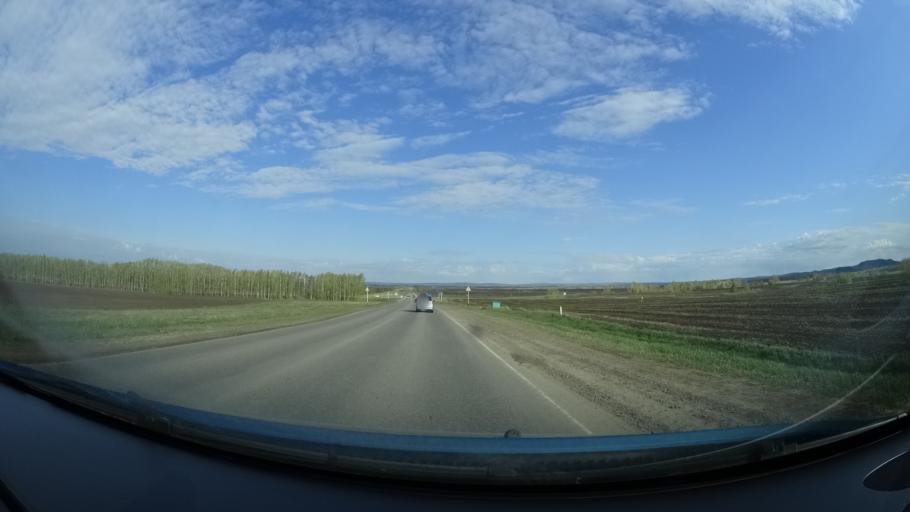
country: RU
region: Bashkortostan
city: Blagoveshchensk
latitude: 55.1837
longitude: 55.8505
